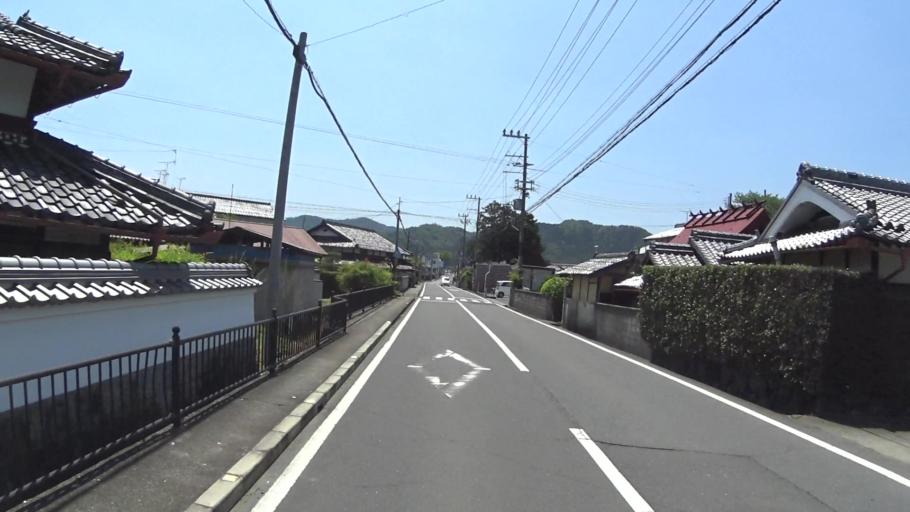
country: JP
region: Kyoto
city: Kameoka
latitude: 35.0754
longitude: 135.5412
